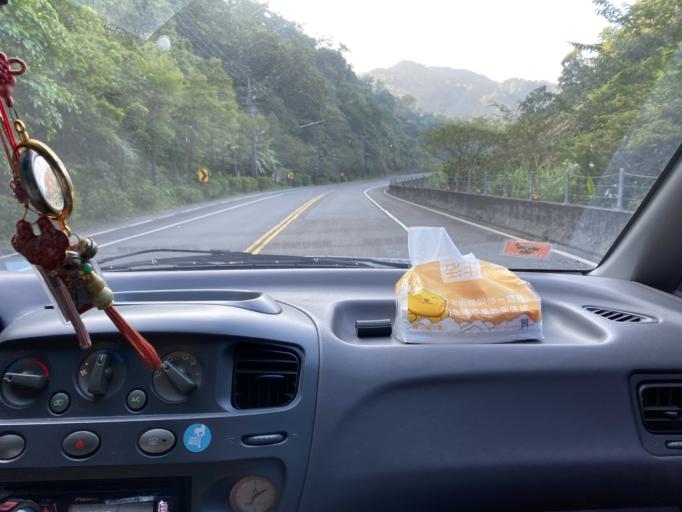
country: TW
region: Taiwan
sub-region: Keelung
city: Keelung
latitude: 25.0295
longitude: 121.7799
